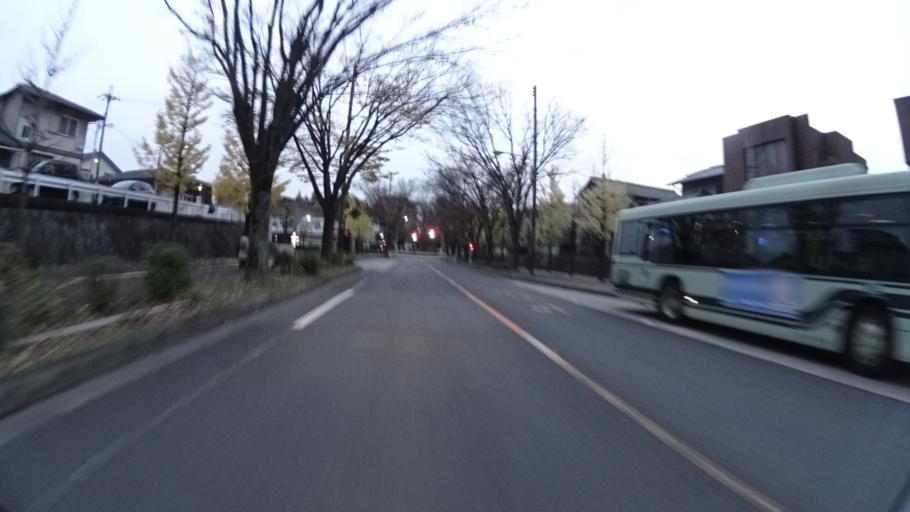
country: JP
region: Kyoto
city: Muko
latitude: 34.9574
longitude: 135.6700
